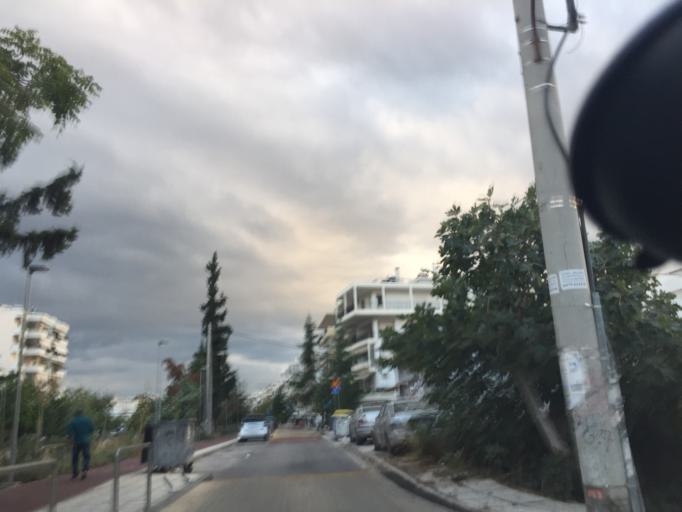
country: GR
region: Attica
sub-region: Nomarchia Athinas
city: Moskhaton
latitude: 37.9495
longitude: 23.6855
